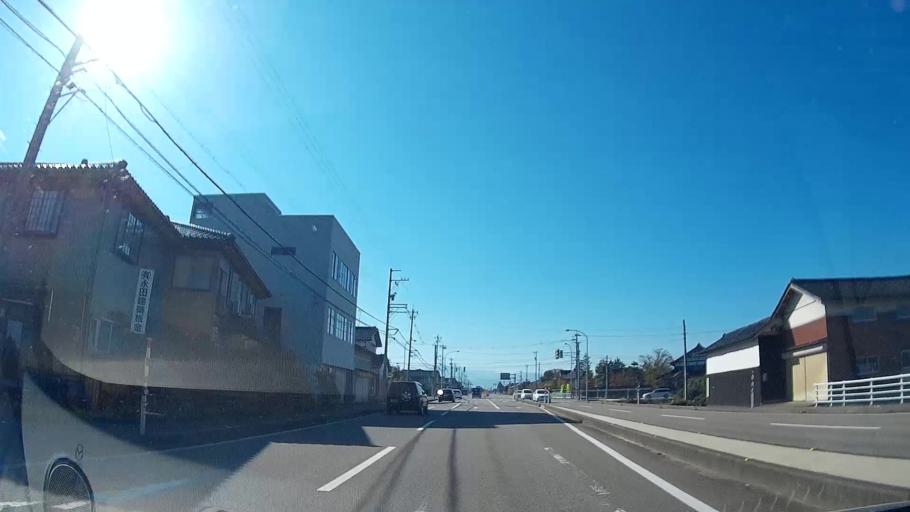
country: JP
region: Toyama
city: Nanto-shi
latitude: 36.6215
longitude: 136.9424
